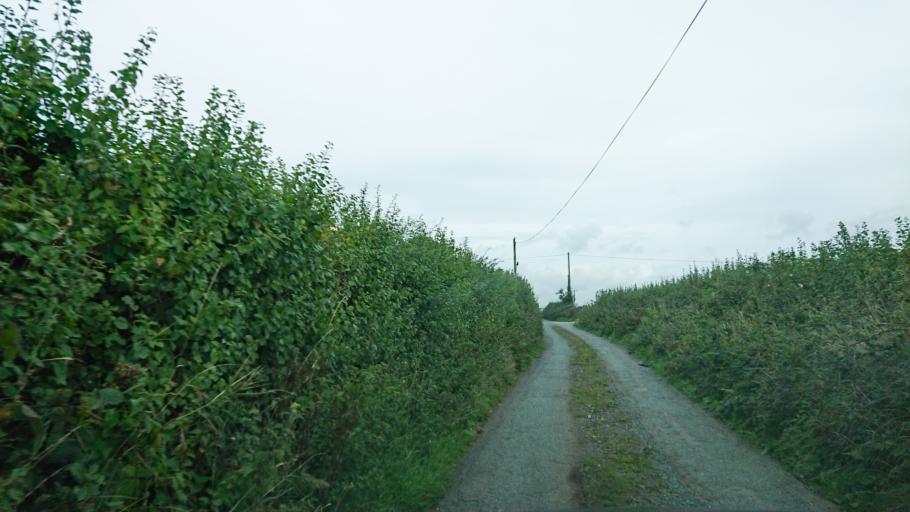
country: IE
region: Munster
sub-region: Waterford
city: Dunmore East
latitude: 52.2041
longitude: -7.0458
